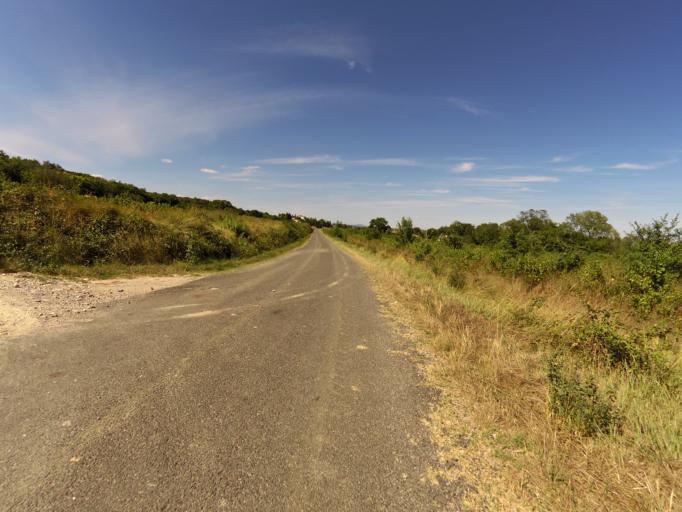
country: FR
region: Languedoc-Roussillon
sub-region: Departement du Gard
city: Quissac
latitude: 43.9492
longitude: 4.0498
